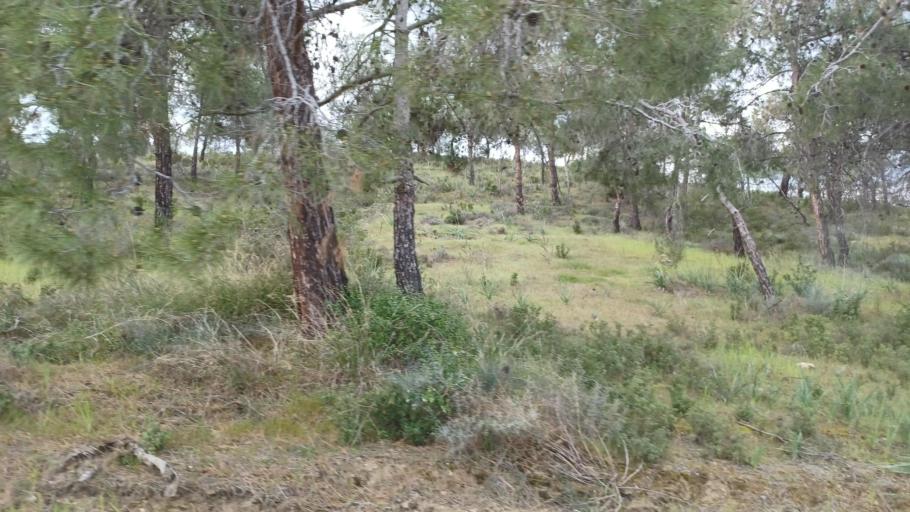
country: CY
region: Lefkosia
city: Kakopetria
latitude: 35.0745
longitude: 32.9583
